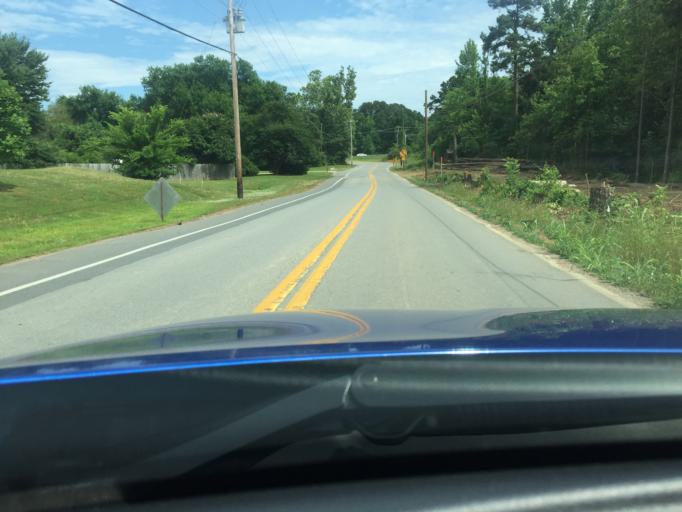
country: US
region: Arkansas
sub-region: Pulaski County
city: Maumelle
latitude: 34.8044
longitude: -92.4350
